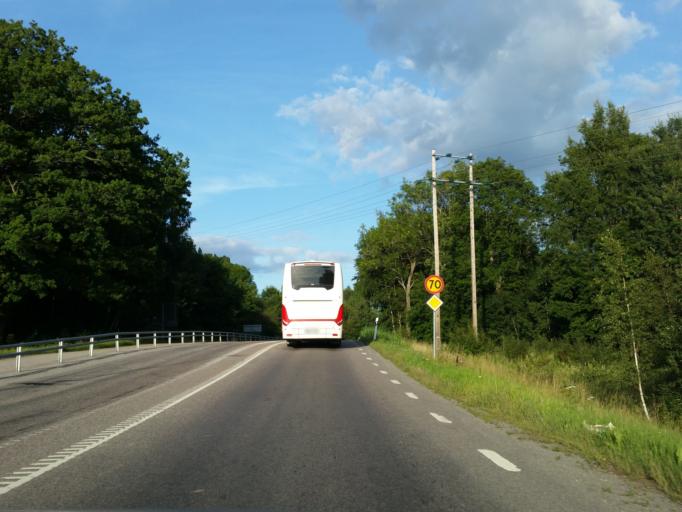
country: SE
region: Stockholm
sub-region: Sodertalje Kommun
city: Pershagen
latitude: 59.0871
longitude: 17.5854
